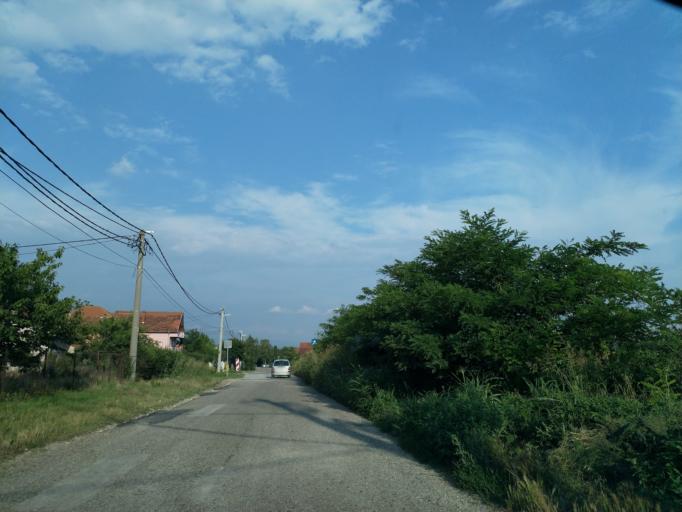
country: RS
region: Central Serbia
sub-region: Pomoravski Okrug
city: Jagodina
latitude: 43.9774
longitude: 21.2370
